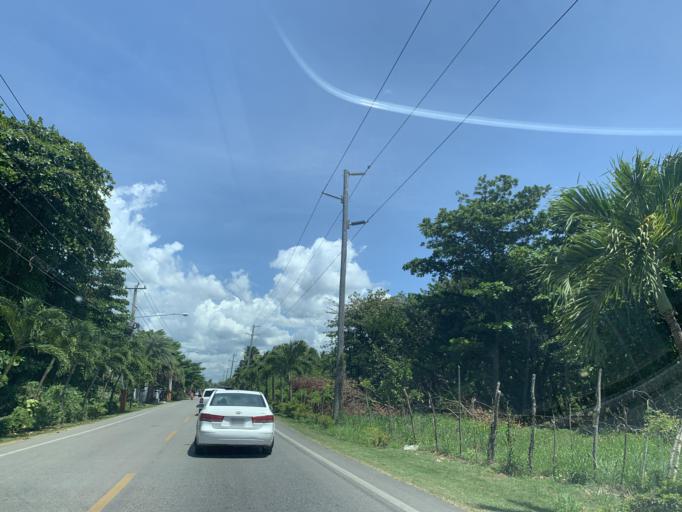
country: DO
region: Puerto Plata
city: Cabarete
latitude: 19.7420
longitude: -70.3930
